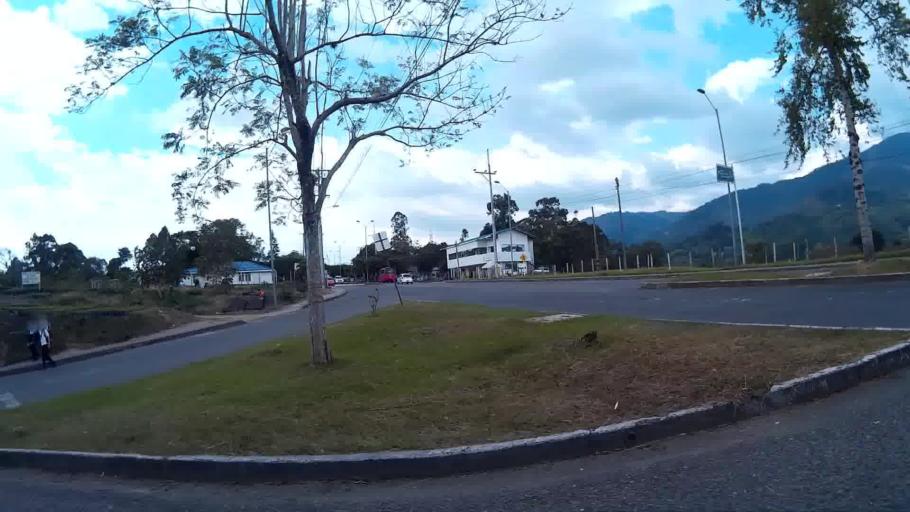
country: CO
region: Quindio
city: Calarca
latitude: 4.5590
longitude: -75.6478
